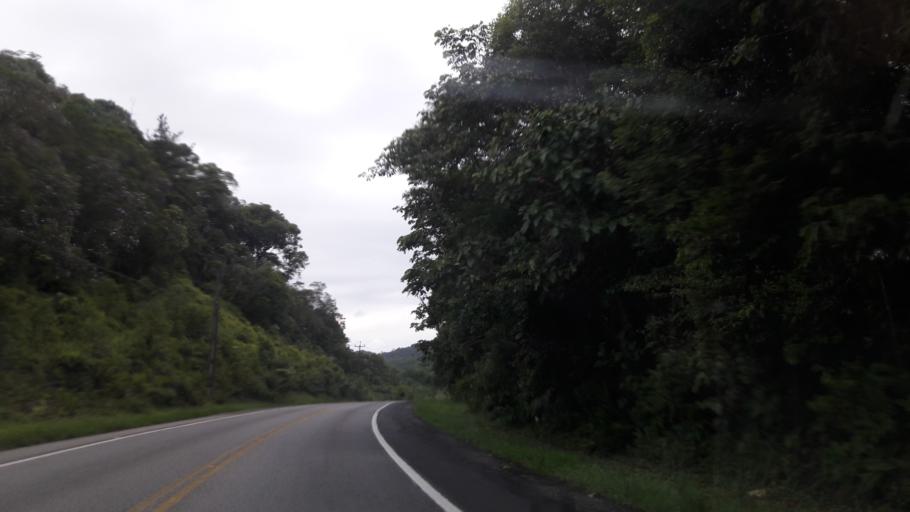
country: BR
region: Parana
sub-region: Antonina
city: Antonina
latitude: -25.4511
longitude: -48.8055
